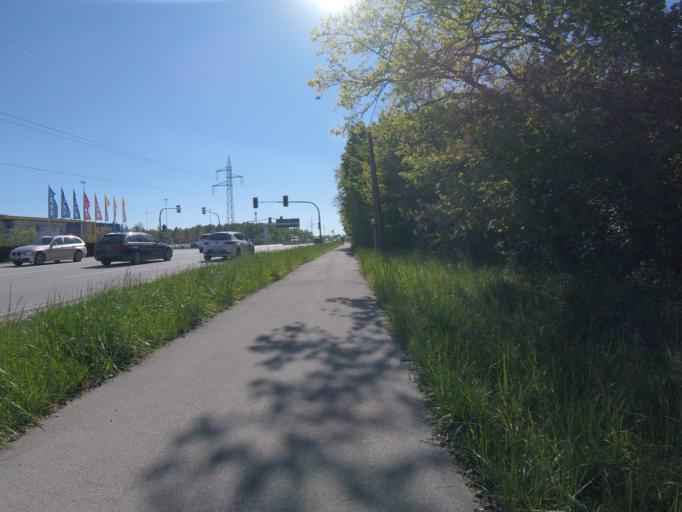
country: DE
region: Bavaria
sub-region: Upper Bavaria
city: Ottobrunn
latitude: 48.0424
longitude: 11.6583
